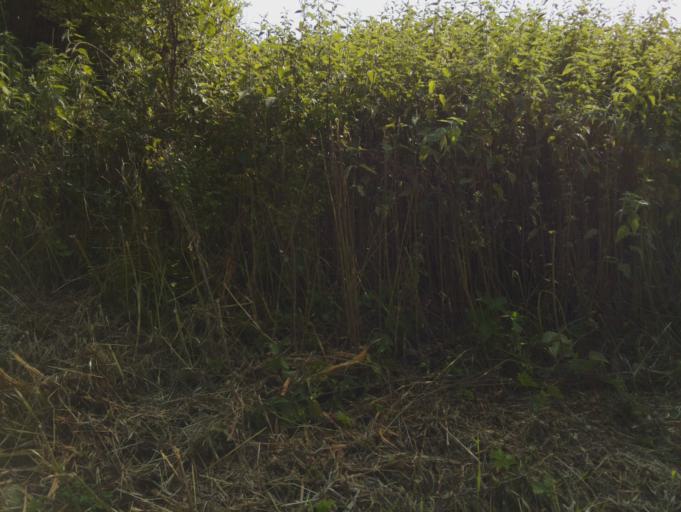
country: CH
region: Zurich
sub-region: Bezirk Andelfingen
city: Grossandelfingen
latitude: 47.5788
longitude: 8.6737
